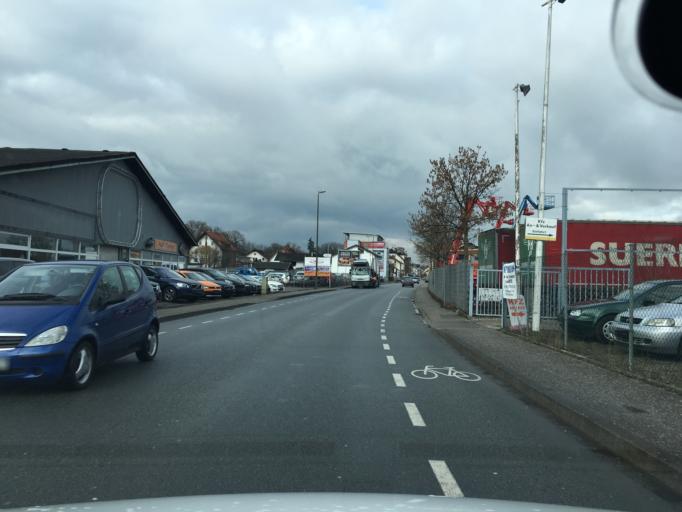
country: DE
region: Bavaria
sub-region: Upper Bavaria
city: Kolbermoor
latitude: 47.8490
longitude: 12.0747
